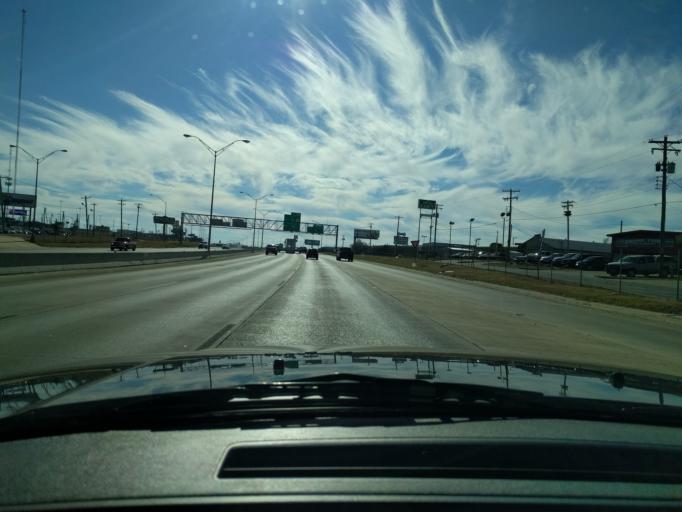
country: US
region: Oklahoma
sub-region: Cleveland County
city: Moore
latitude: 35.4041
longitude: -97.4948
